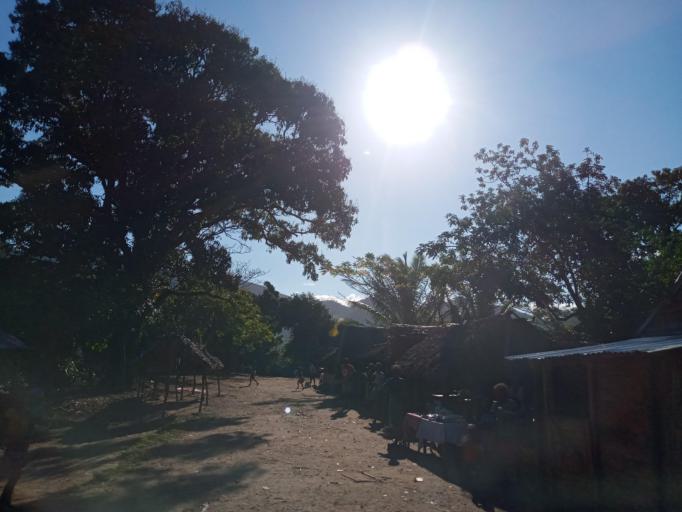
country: MG
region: Anosy
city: Fort Dauphin
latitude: -24.8250
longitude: 47.0443
